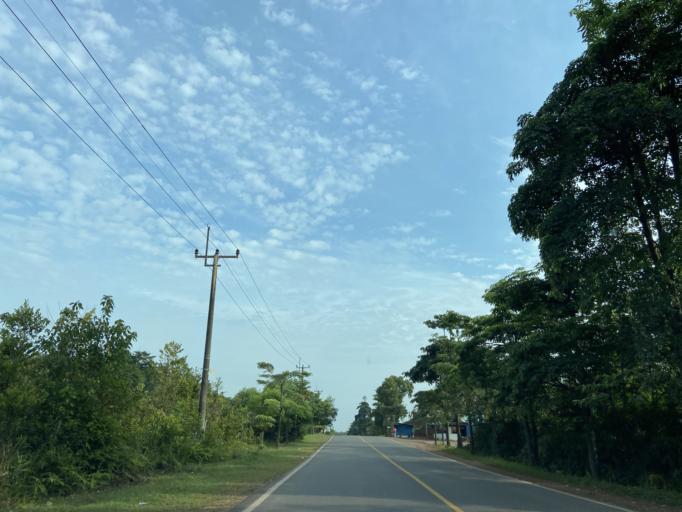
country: ID
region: Riau Islands
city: Tanjungpinang
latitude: 0.9090
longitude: 104.1233
